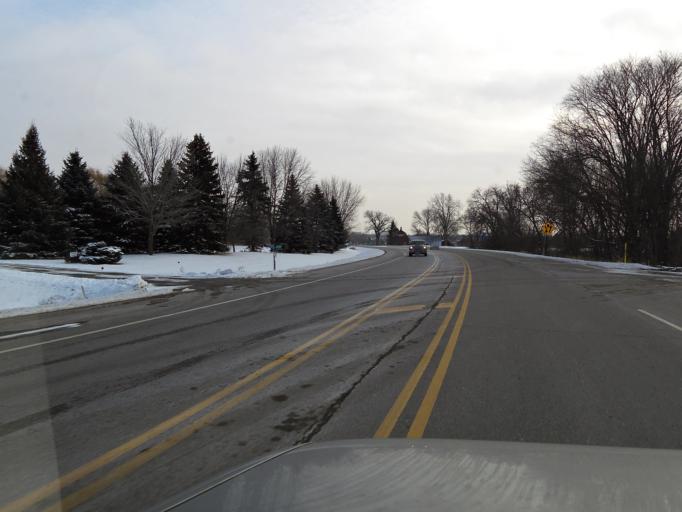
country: US
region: Minnesota
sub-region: Scott County
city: Shakopee
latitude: 44.7516
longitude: -93.5053
